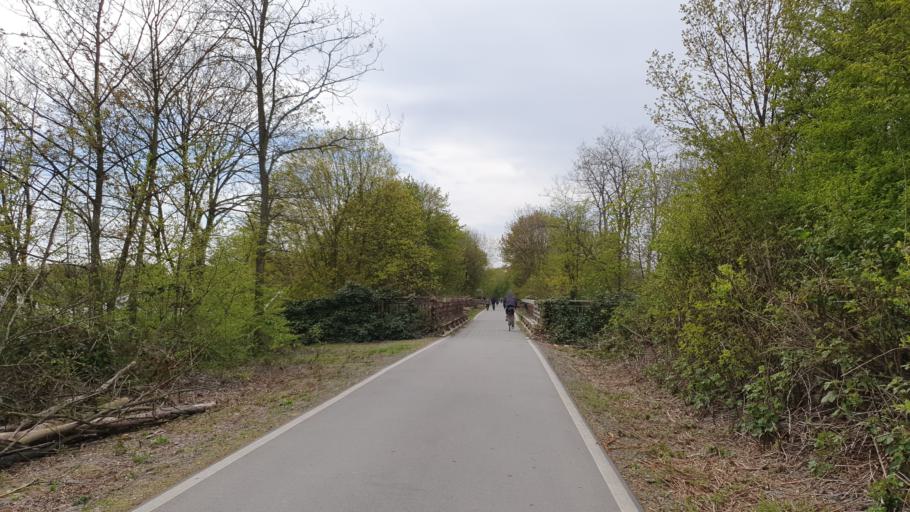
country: DE
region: North Rhine-Westphalia
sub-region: Regierungsbezirk Dusseldorf
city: Oberhausen
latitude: 51.4993
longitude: 6.8370
